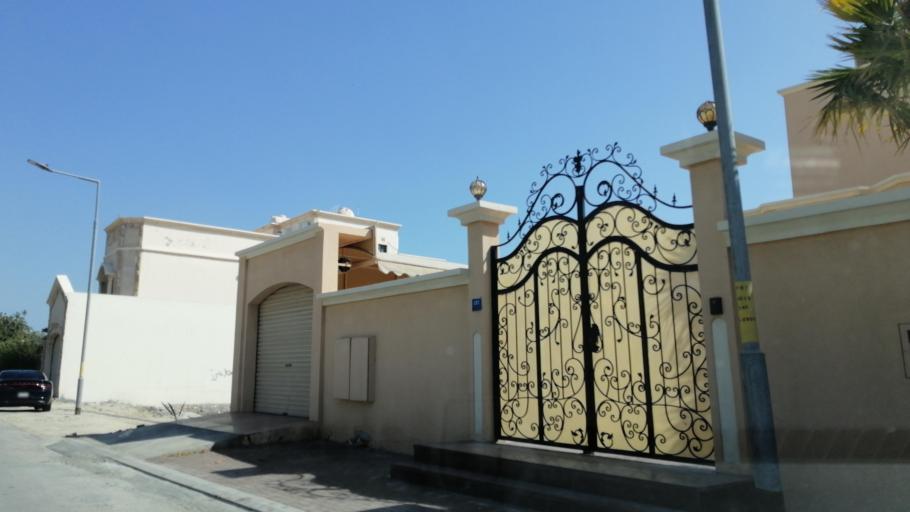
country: BH
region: Muharraq
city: Al Hadd
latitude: 26.2459
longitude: 50.6363
